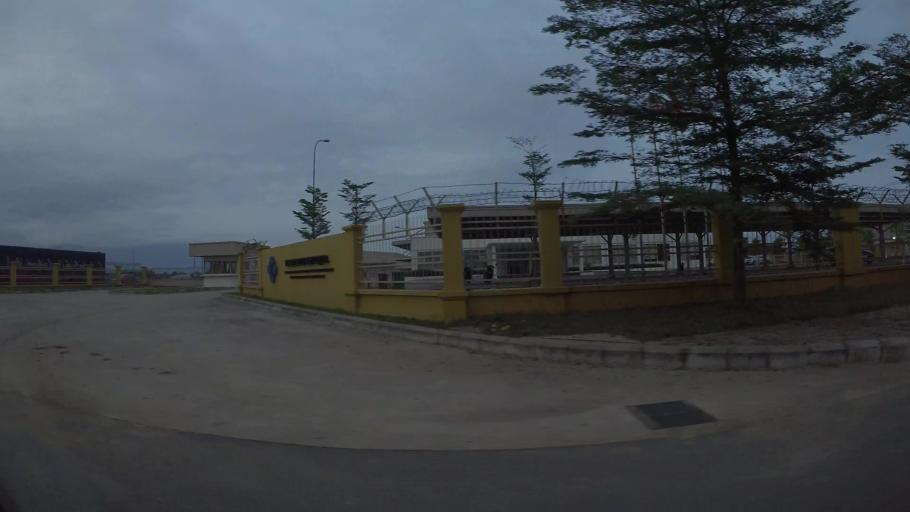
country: VN
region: Da Nang
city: Lien Chieu
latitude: 16.0857
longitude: 108.1142
